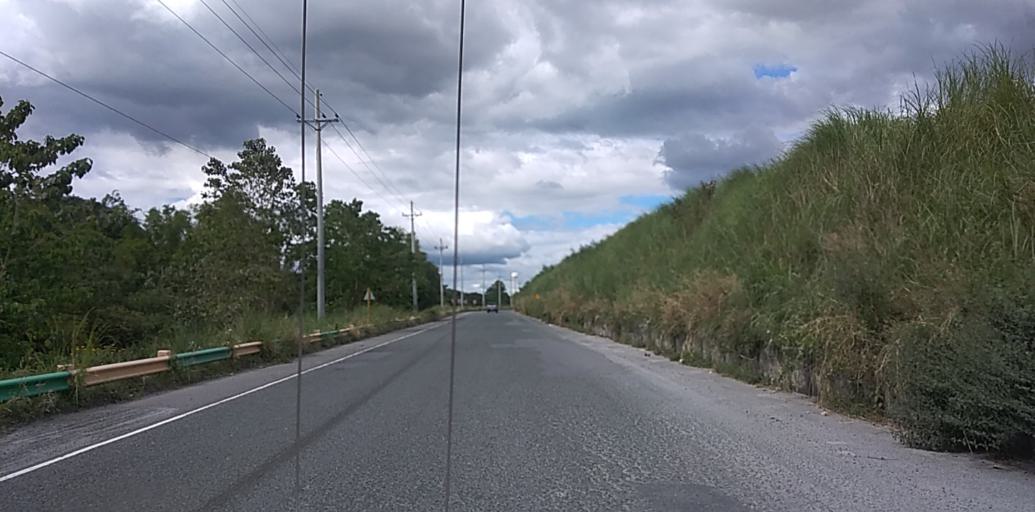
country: PH
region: Central Luzon
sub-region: Province of Pampanga
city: Dolores
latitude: 15.1045
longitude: 120.5217
